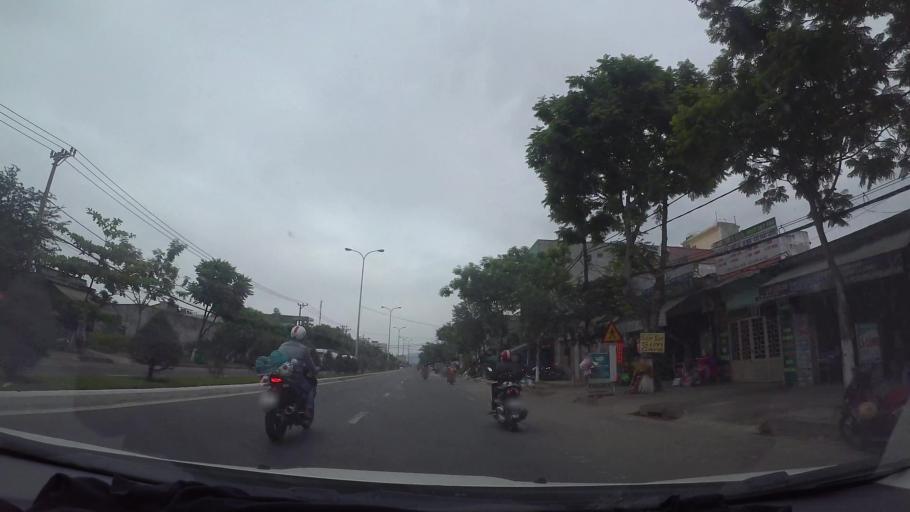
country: VN
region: Da Nang
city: Lien Chieu
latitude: 16.0884
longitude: 108.1435
